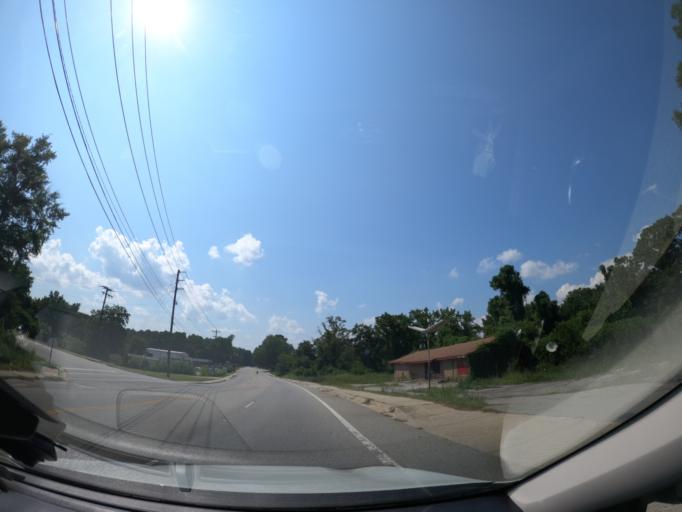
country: US
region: South Carolina
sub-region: Richland County
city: Forest Acres
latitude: 33.9343
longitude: -80.9719
